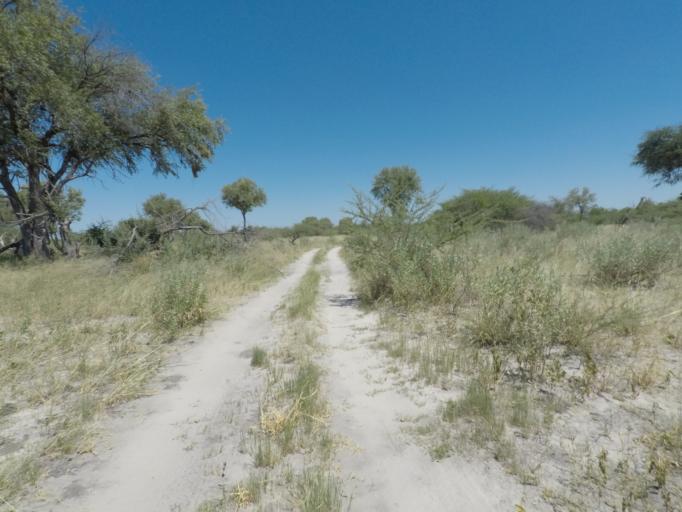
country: BW
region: North West
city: Maun
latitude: -19.4490
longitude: 23.5565
